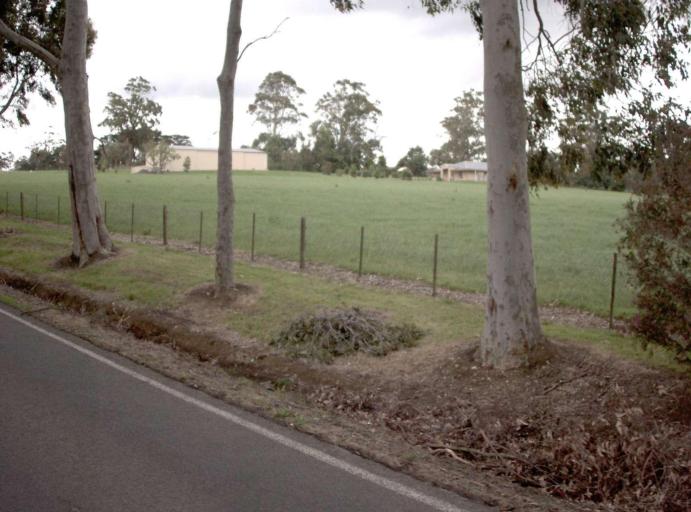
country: AU
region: Victoria
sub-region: Baw Baw
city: Warragul
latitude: -38.1014
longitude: 145.9719
